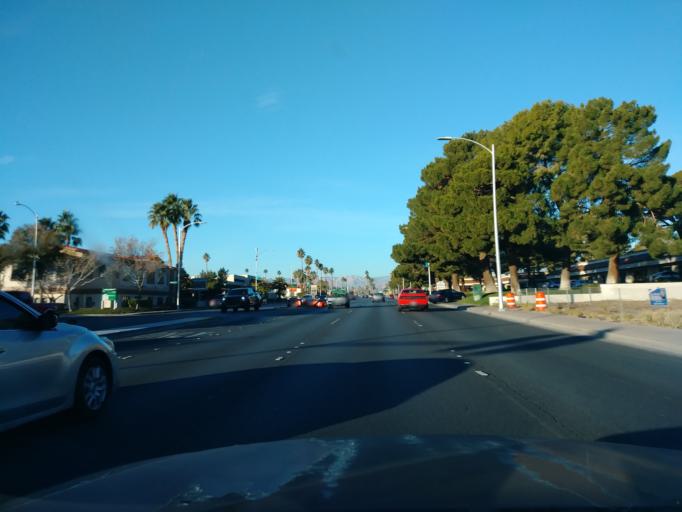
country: US
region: Nevada
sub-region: Clark County
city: Las Vegas
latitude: 36.1590
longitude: -115.1785
